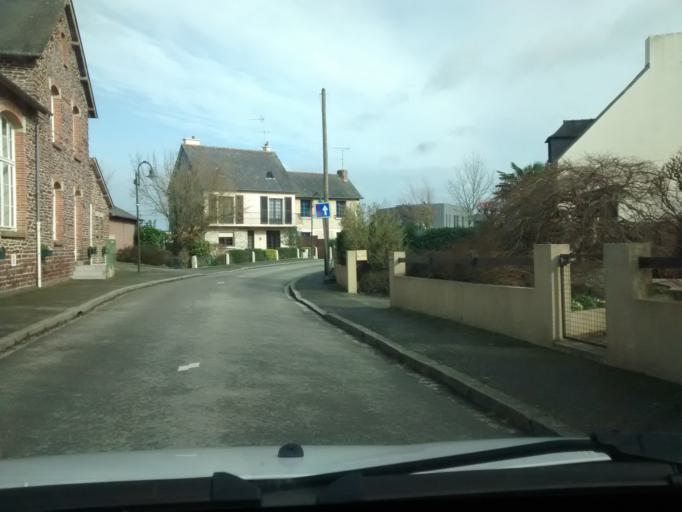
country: FR
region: Brittany
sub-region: Departement d'Ille-et-Vilaine
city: Nouvoitou
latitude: 48.0425
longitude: -1.5462
